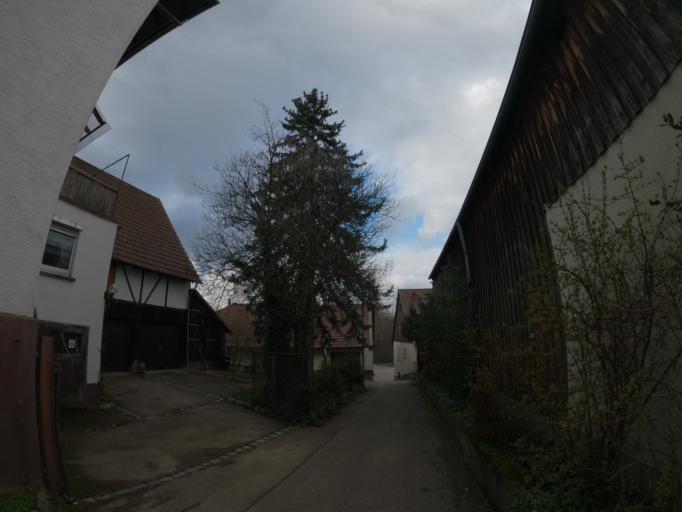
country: DE
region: Baden-Wuerttemberg
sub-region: Regierungsbezirk Stuttgart
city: Schlat
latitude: 48.6529
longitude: 9.7032
